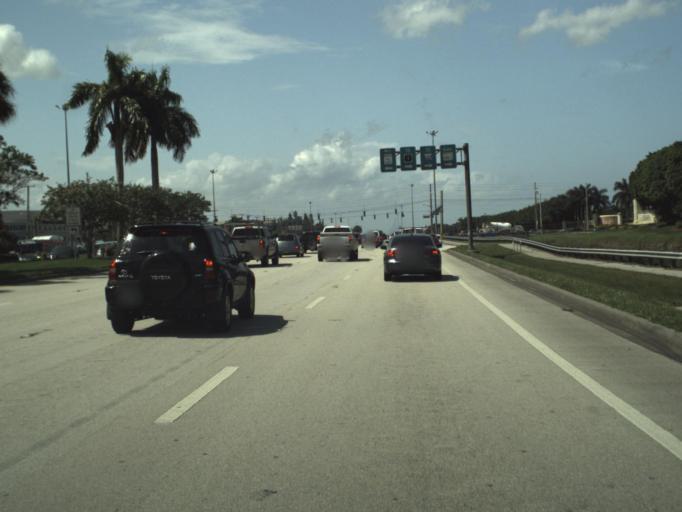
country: US
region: Florida
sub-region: Palm Beach County
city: Wellington
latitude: 26.6484
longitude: -80.2034
